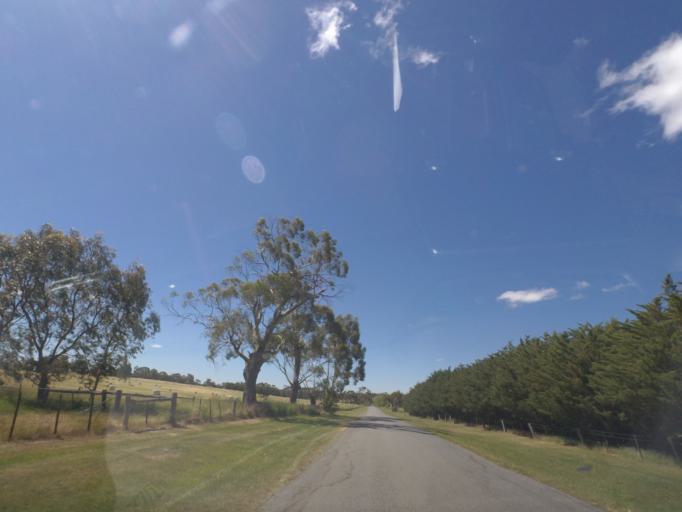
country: AU
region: Victoria
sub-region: Mount Alexander
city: Castlemaine
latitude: -37.3011
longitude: 144.4439
